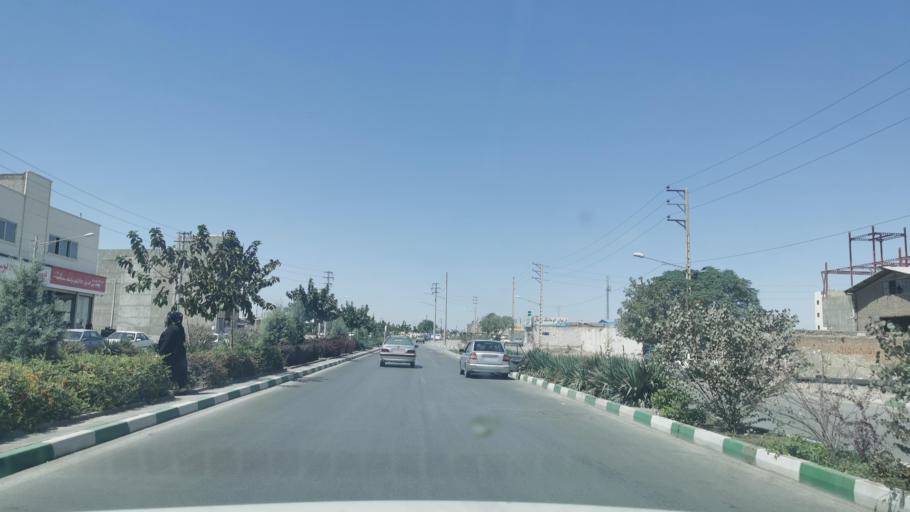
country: IR
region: Razavi Khorasan
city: Mashhad
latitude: 36.3519
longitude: 59.5734
